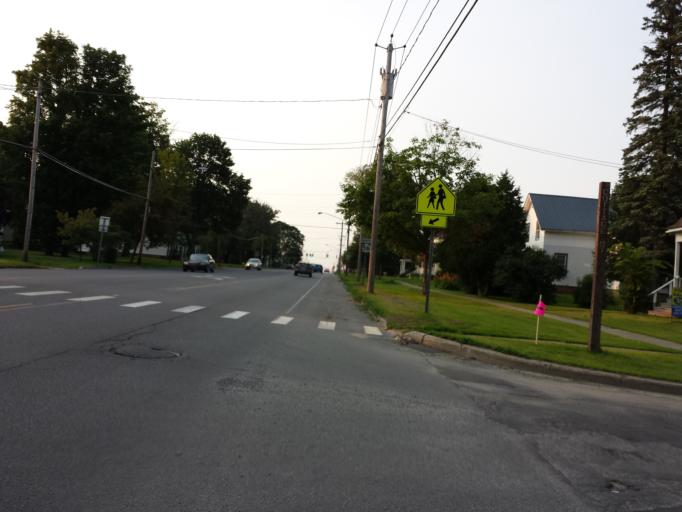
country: US
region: New York
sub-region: St. Lawrence County
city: Potsdam
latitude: 44.6761
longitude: -74.9868
